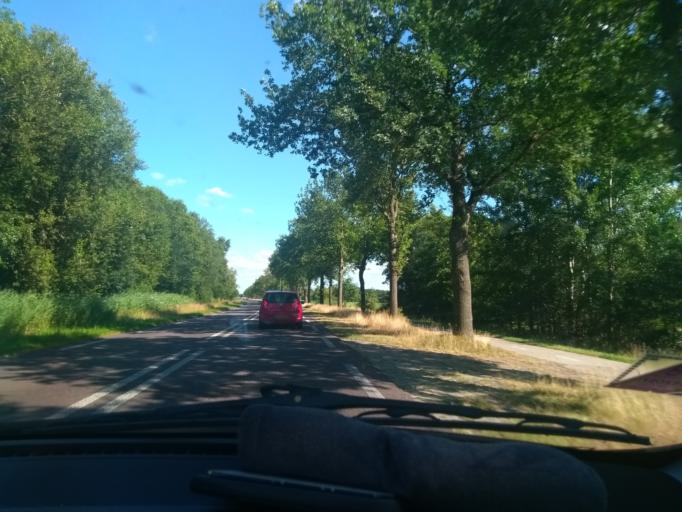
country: NL
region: Drenthe
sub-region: Gemeente Tynaarlo
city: Vries
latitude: 53.1084
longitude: 6.5228
